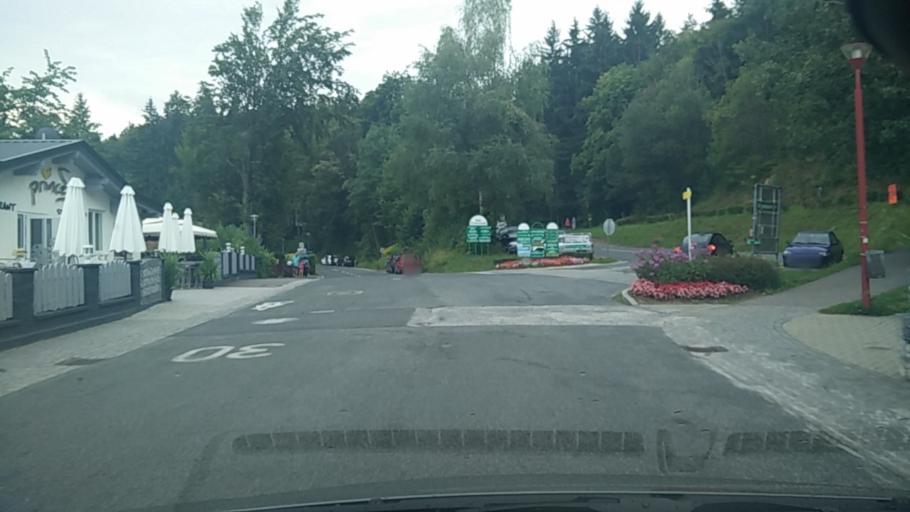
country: AT
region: Carinthia
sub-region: Politischer Bezirk Volkermarkt
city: Sittersdorf
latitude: 46.6031
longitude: 14.5718
